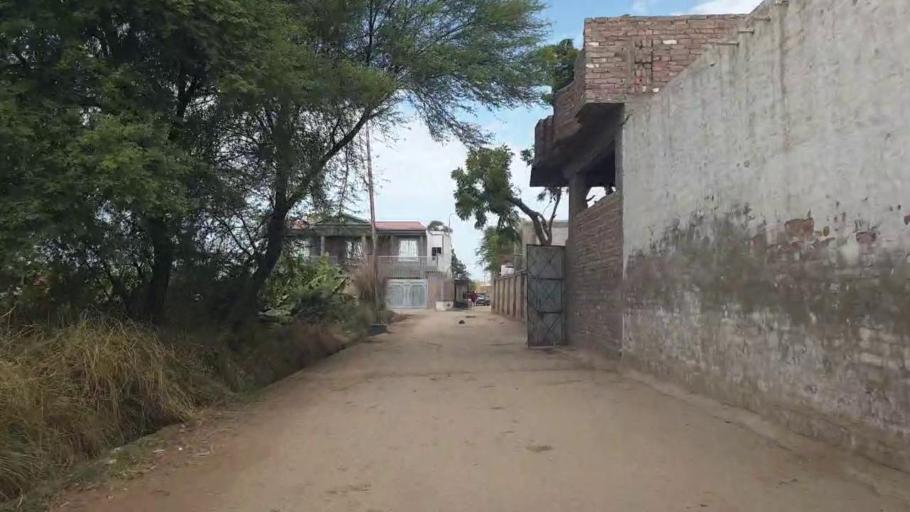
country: PK
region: Sindh
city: Sakrand
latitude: 25.9911
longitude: 68.3575
